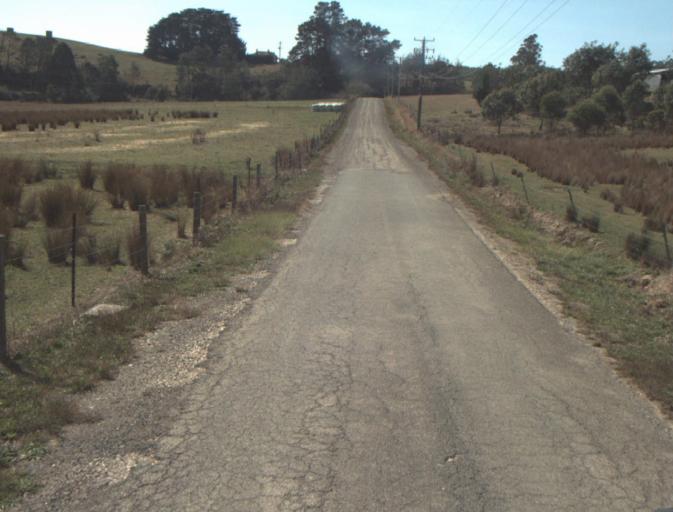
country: AU
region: Tasmania
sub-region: Launceston
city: Mayfield
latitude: -41.2265
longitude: 147.2365
